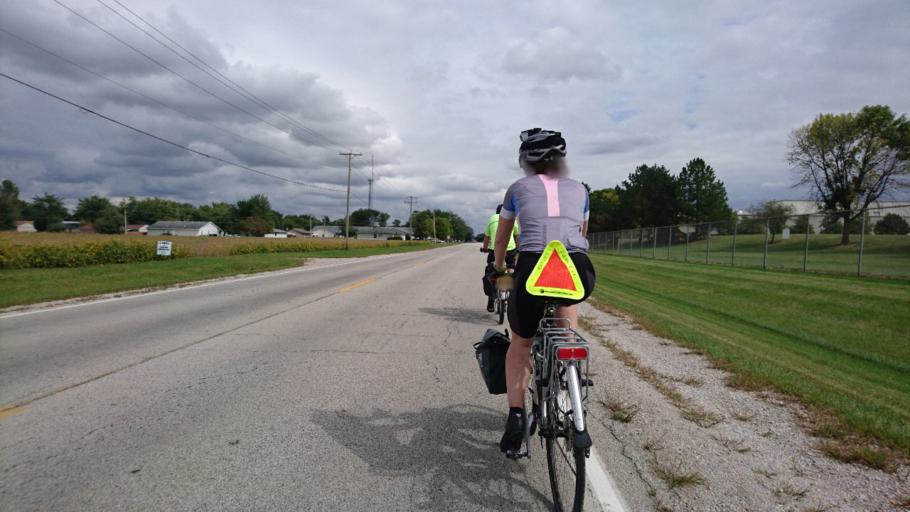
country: US
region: Illinois
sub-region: Livingston County
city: Pontiac
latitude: 40.8881
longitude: -88.6563
